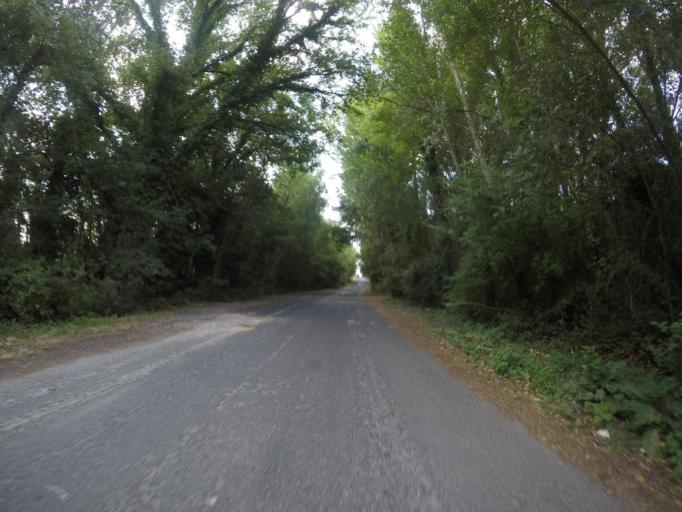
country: FR
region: Languedoc-Roussillon
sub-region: Departement des Pyrenees-Orientales
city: Ille-sur-Tet
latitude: 42.6916
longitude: 2.6545
